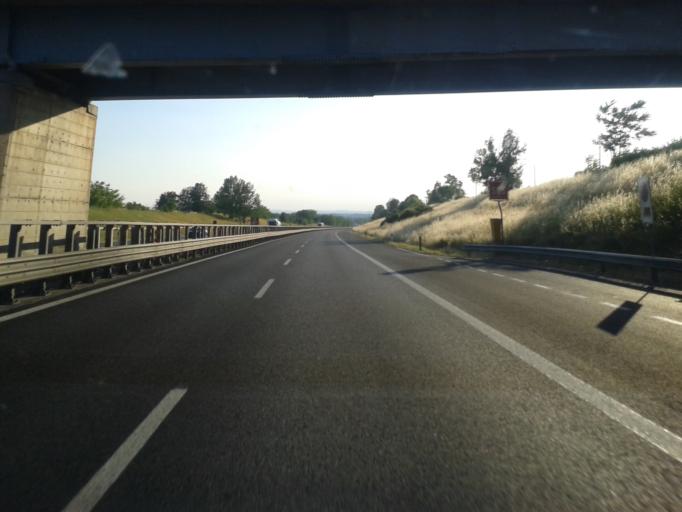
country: IT
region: Piedmont
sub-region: Provincia di Alessandria
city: Fresonara
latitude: 44.7781
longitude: 8.6951
